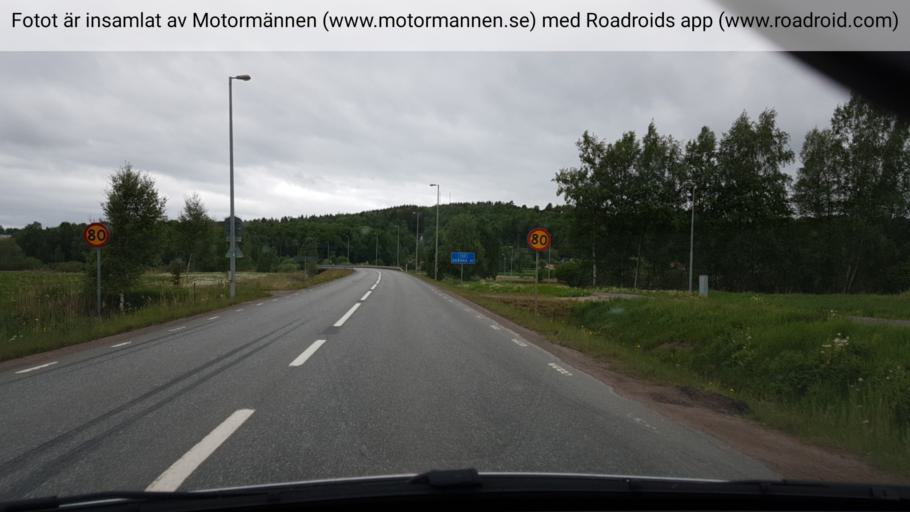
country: SE
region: Joenkoeping
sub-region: Tranas Kommun
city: Tranas
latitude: 57.9891
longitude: 14.8500
